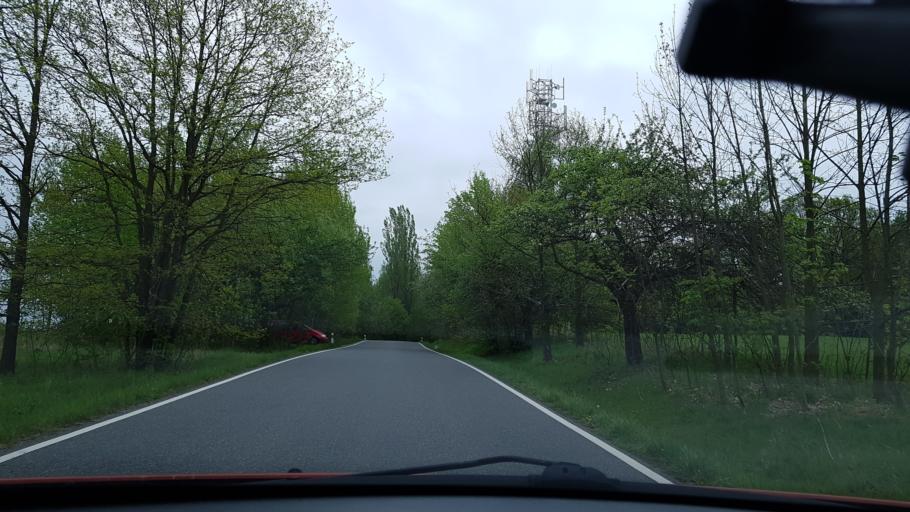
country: CZ
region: Olomoucky
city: Vidnava
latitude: 50.3643
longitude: 17.2003
